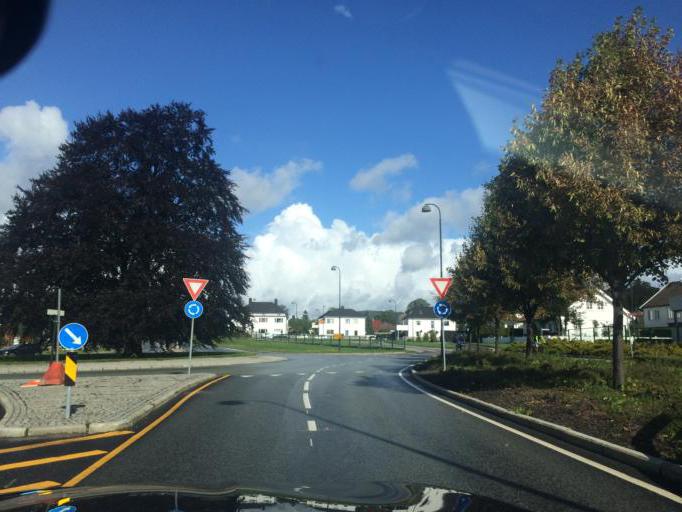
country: NO
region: Vest-Agder
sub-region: Kristiansand
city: Kristiansand
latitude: 58.1548
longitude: 8.0039
